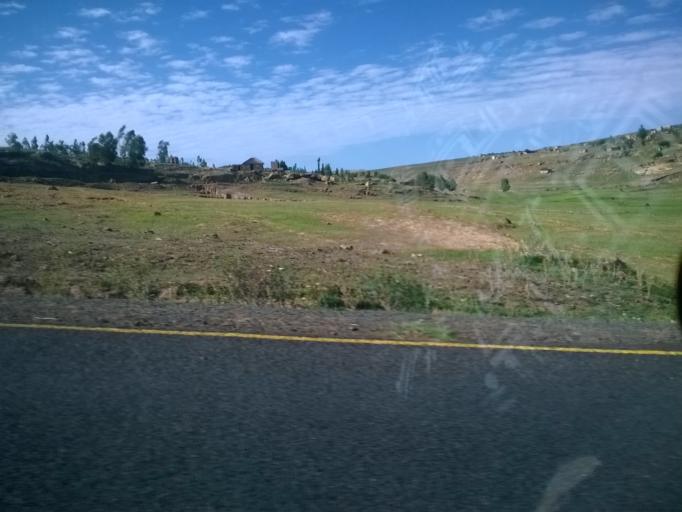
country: LS
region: Berea
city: Teyateyaneng
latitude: -29.0873
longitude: 27.8829
